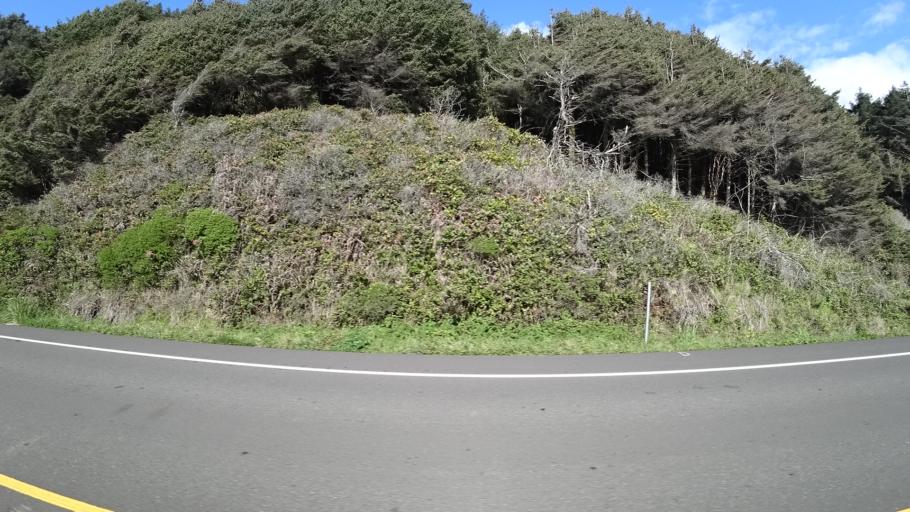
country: US
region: Oregon
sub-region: Lincoln County
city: Waldport
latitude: 44.2369
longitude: -124.1103
